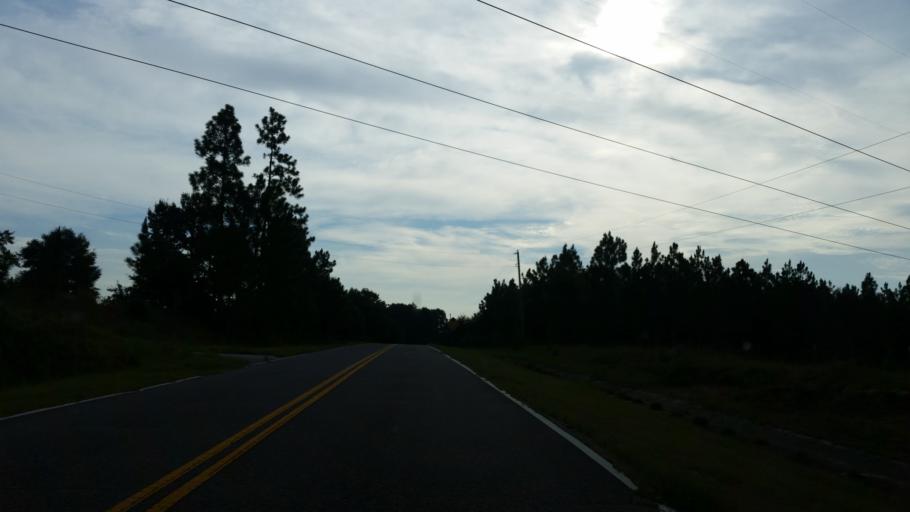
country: US
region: Florida
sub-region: Escambia County
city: Molino
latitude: 30.7731
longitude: -87.4876
